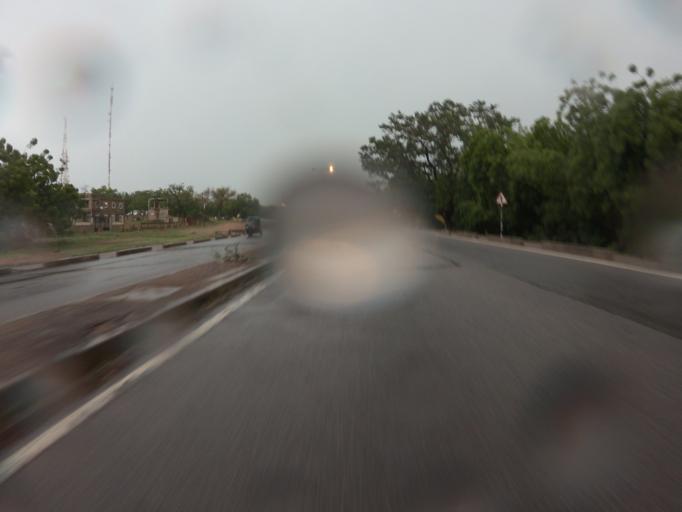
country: GH
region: Upper East
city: Bolgatanga
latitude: 10.8001
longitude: -0.8606
